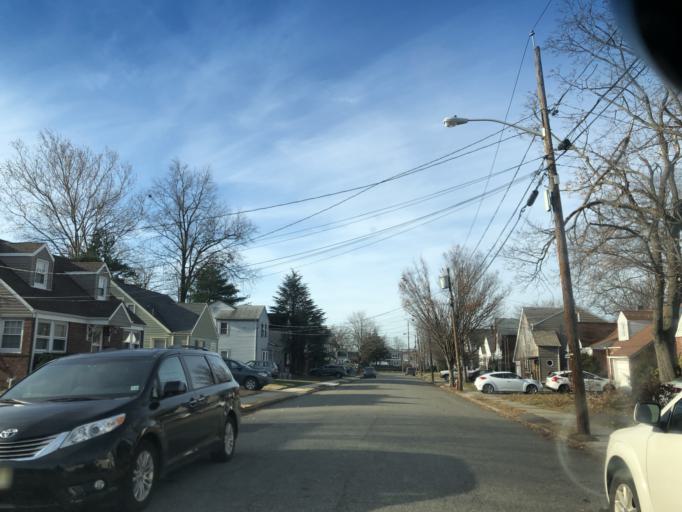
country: US
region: New Jersey
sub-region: Bergen County
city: Fair Lawn
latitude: 40.9297
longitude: -74.1292
